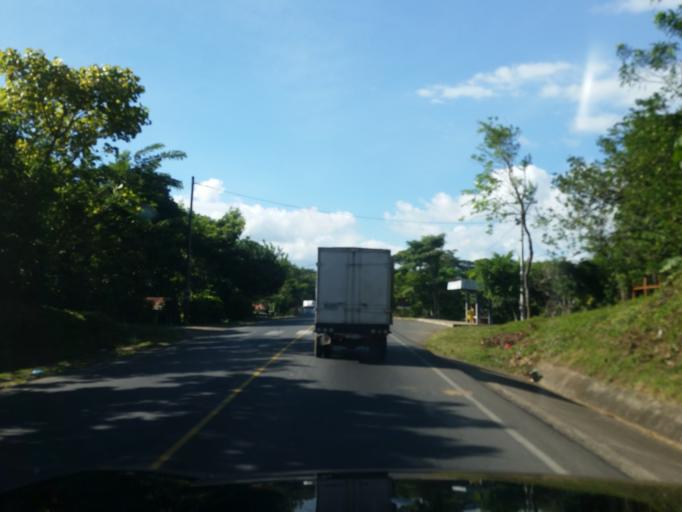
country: NI
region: Masaya
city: San Juan de Oriente
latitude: 11.9067
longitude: -86.0725
